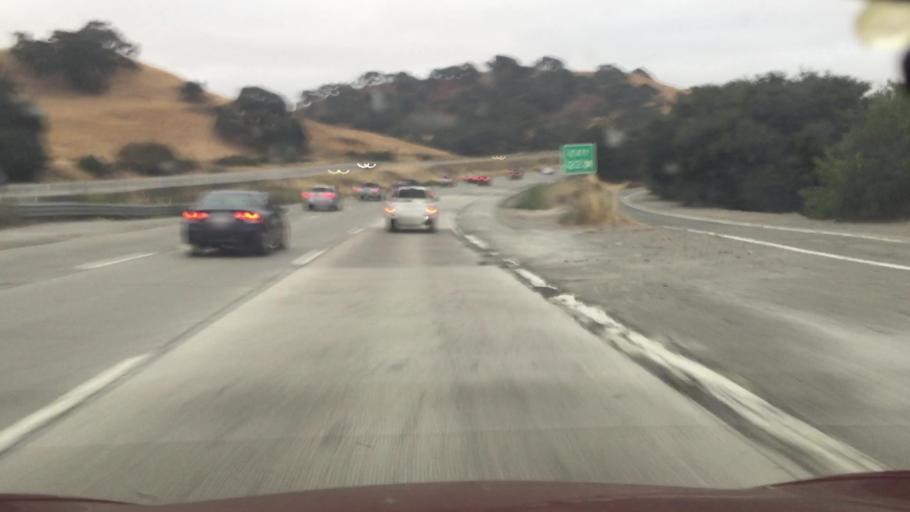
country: US
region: California
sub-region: Alameda County
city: Pleasanton
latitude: 37.6047
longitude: -121.8723
